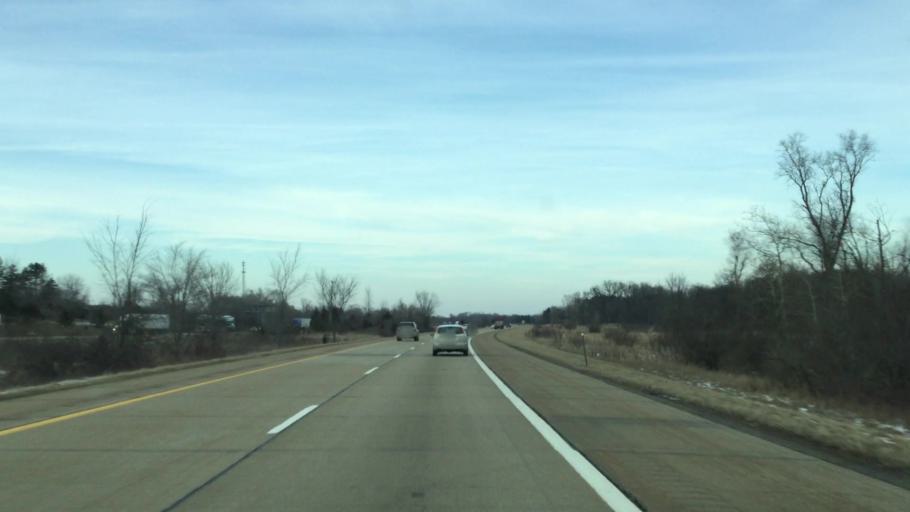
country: US
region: Michigan
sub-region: Eaton County
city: Bellevue
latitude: 42.3697
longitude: -84.9776
